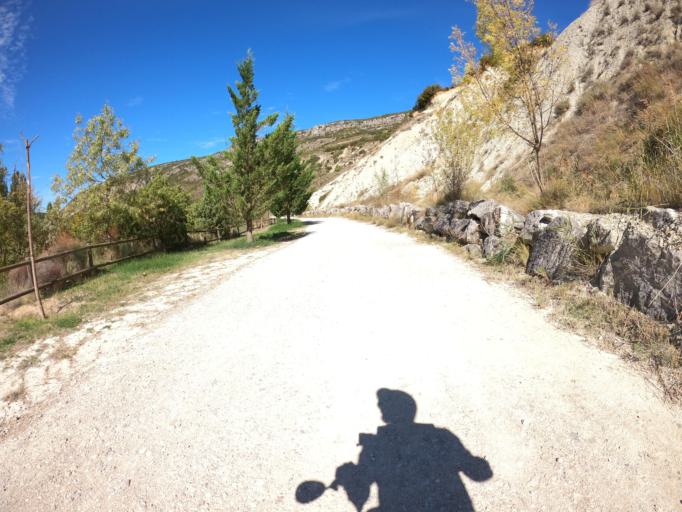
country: ES
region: Navarre
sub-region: Provincia de Navarra
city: Liedena
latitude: 42.6219
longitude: -1.2889
